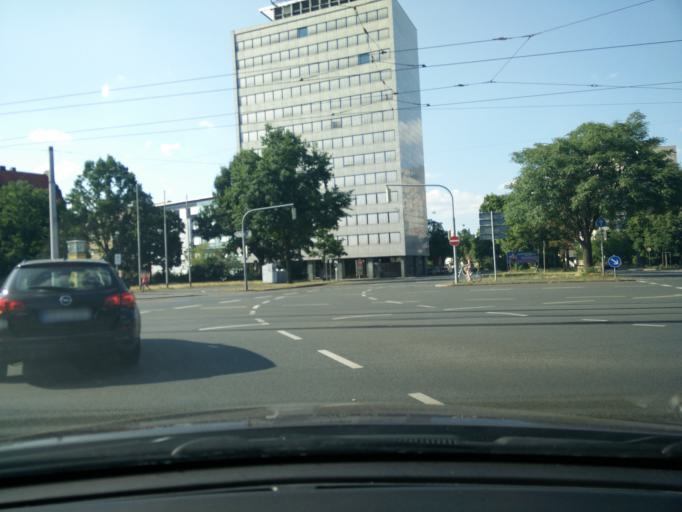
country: DE
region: Bavaria
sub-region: Regierungsbezirk Mittelfranken
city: Nuernberg
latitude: 49.4385
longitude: 11.1030
